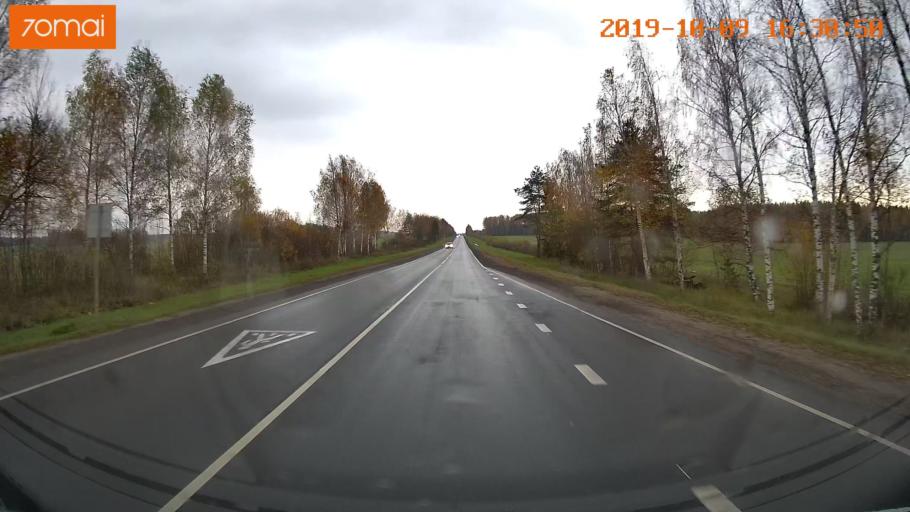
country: RU
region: Kostroma
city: Oktyabr'skiy
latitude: 57.6140
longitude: 40.9447
